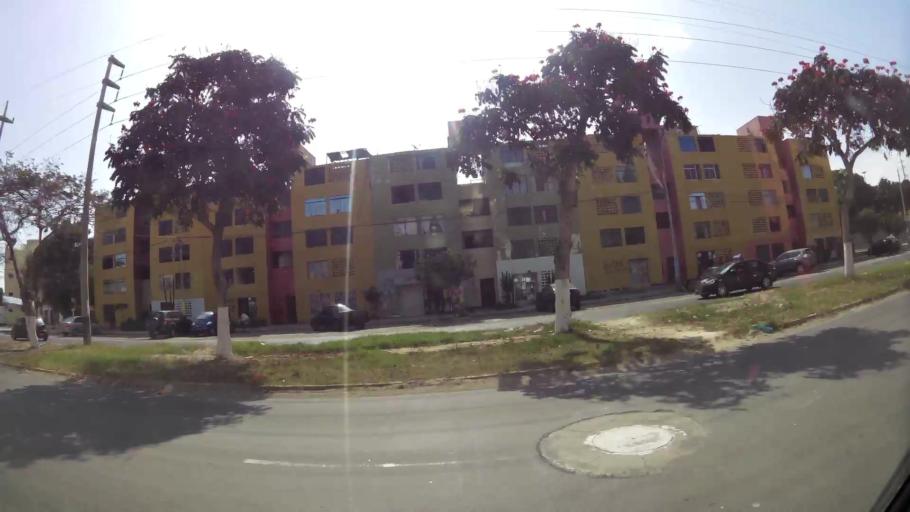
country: PE
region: La Libertad
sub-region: Provincia de Trujillo
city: Trujillo
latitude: -8.1210
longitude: -79.0416
